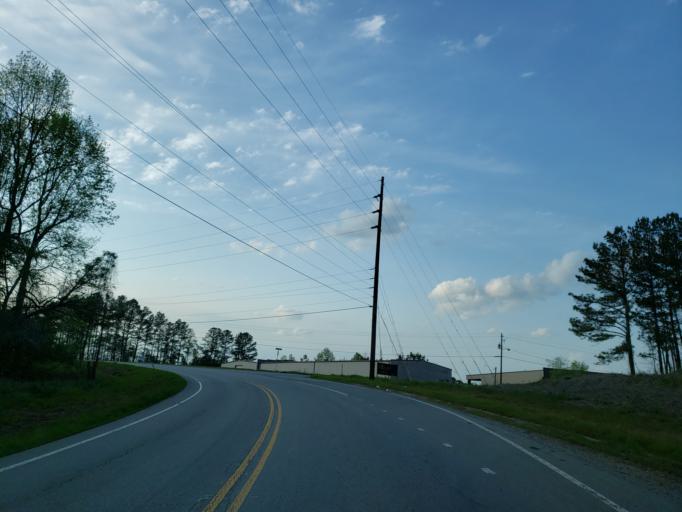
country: US
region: Georgia
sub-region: Cherokee County
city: Ball Ground
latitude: 34.3028
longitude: -84.4001
